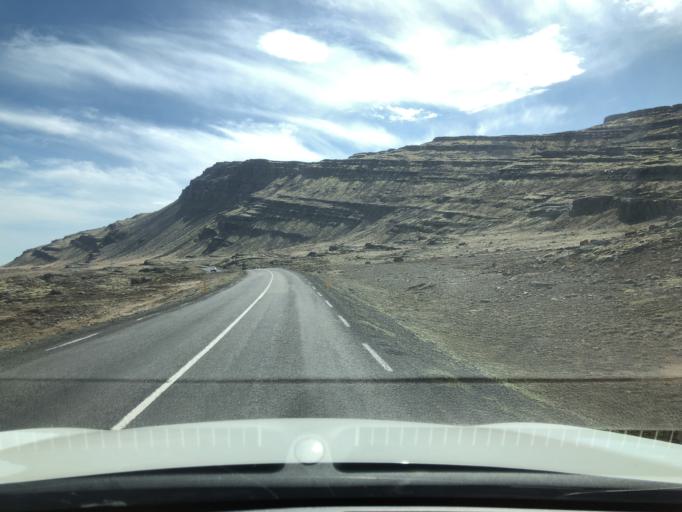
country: IS
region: East
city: Reydarfjoerdur
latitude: 64.6394
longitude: -14.4805
